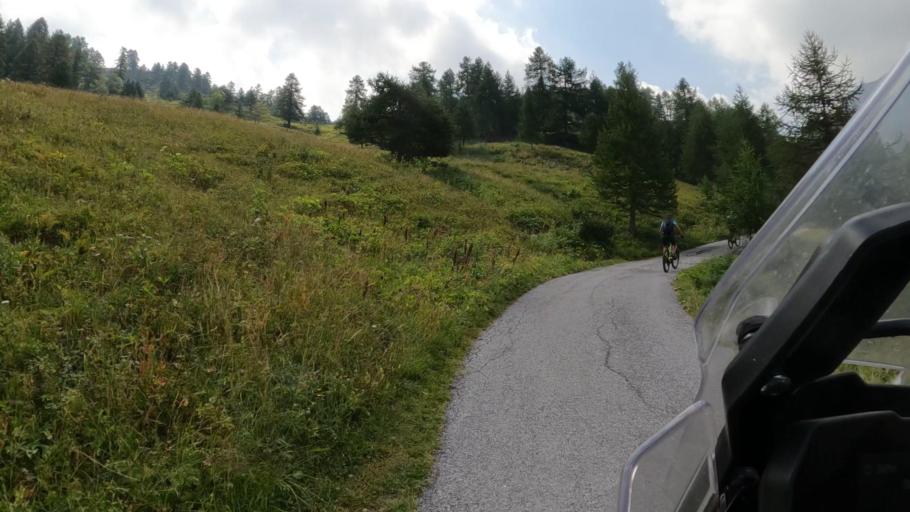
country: IT
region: Piedmont
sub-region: Provincia di Cuneo
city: Marmora
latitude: 44.4178
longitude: 7.1064
